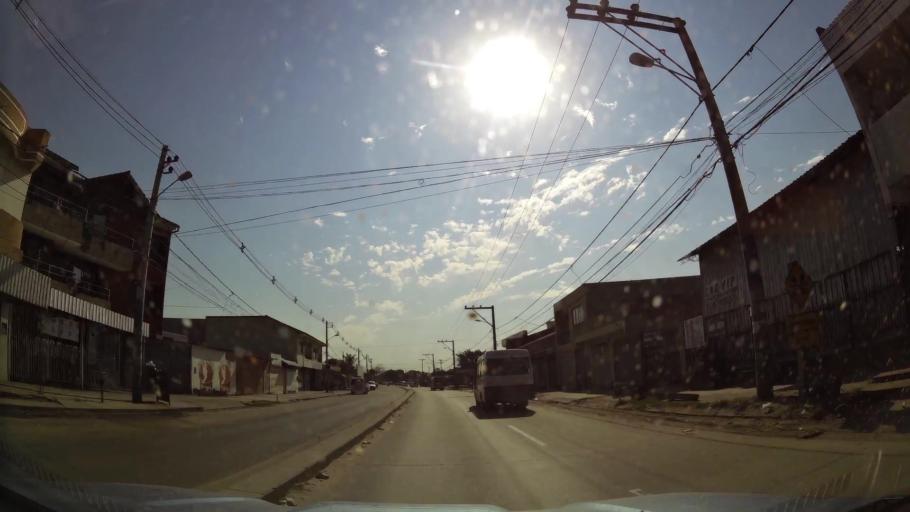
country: BO
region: Santa Cruz
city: Santa Cruz de la Sierra
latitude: -17.8182
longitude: -63.1494
